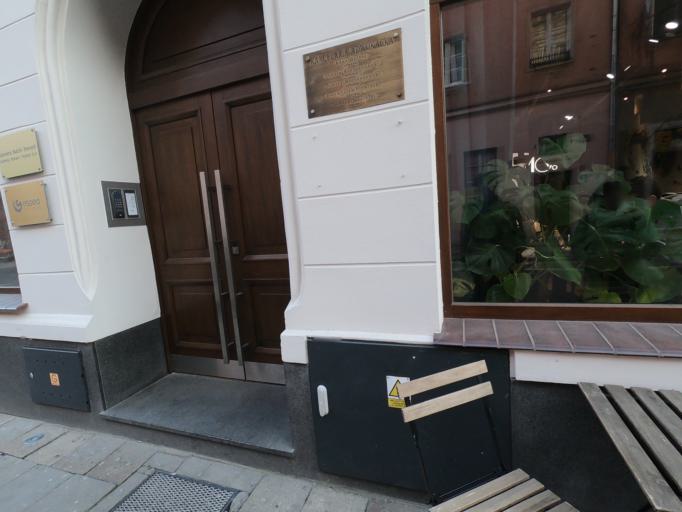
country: PL
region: Greater Poland Voivodeship
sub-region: Poznan
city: Poznan
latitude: 52.4099
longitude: 16.9340
